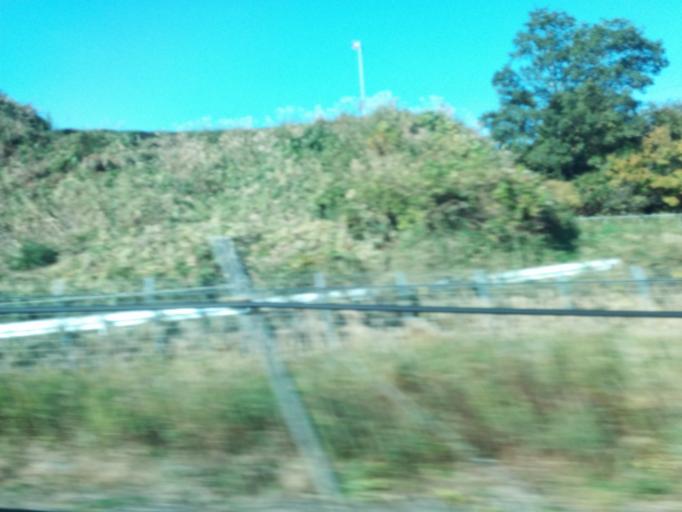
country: JP
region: Shizuoka
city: Kanaya
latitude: 34.7751
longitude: 138.1065
